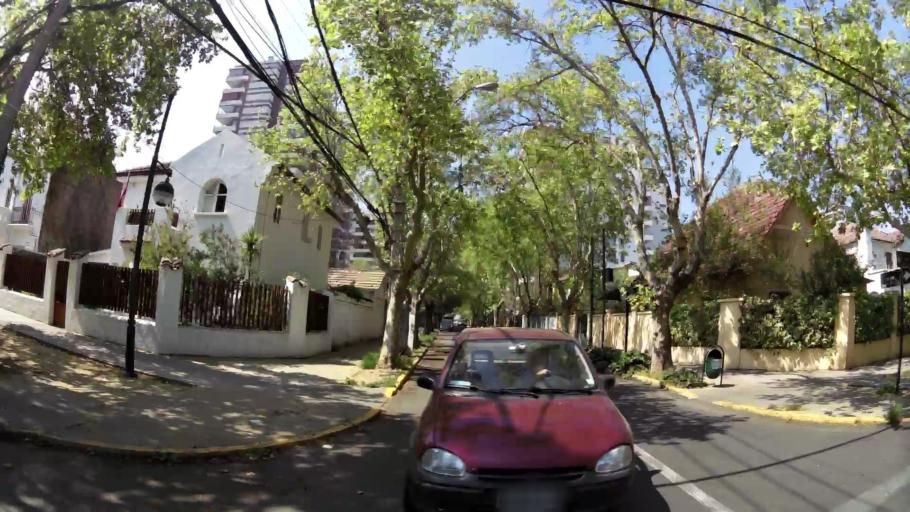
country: CL
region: Santiago Metropolitan
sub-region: Provincia de Santiago
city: Villa Presidente Frei, Nunoa, Santiago, Chile
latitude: -33.4516
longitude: -70.6036
